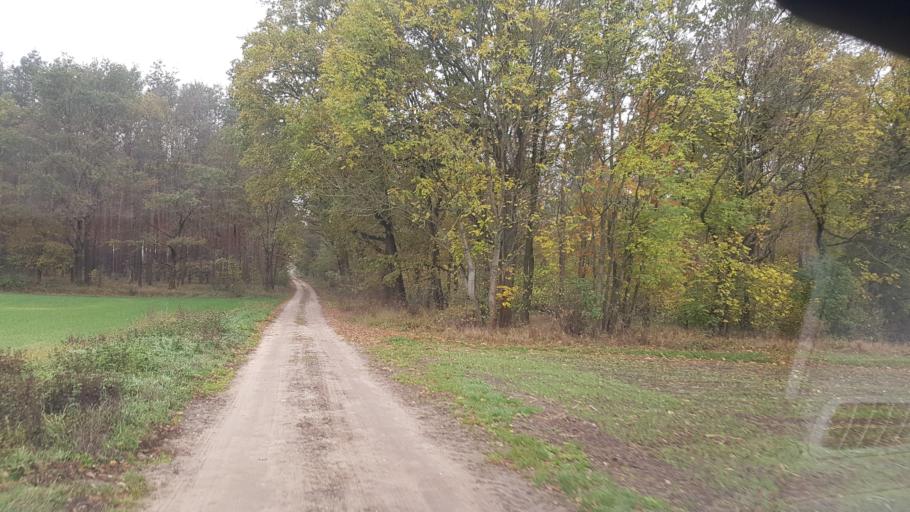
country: DE
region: Brandenburg
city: Schonborn
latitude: 51.6825
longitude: 13.4908
